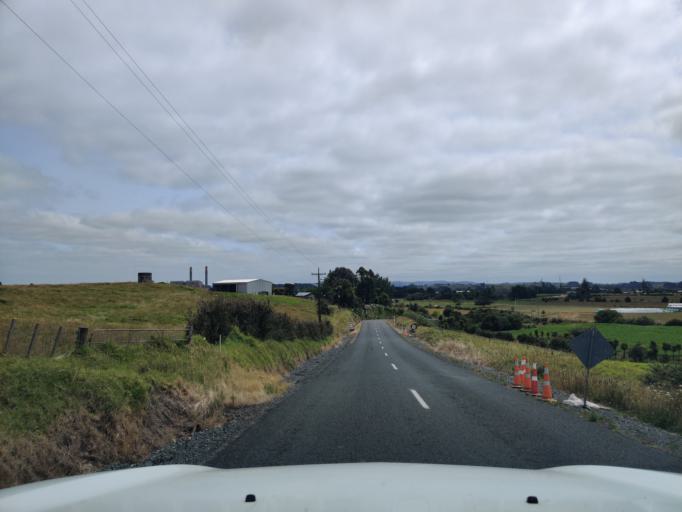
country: NZ
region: Waikato
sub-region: Waikato District
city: Te Kauwhata
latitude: -37.5252
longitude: 175.1725
